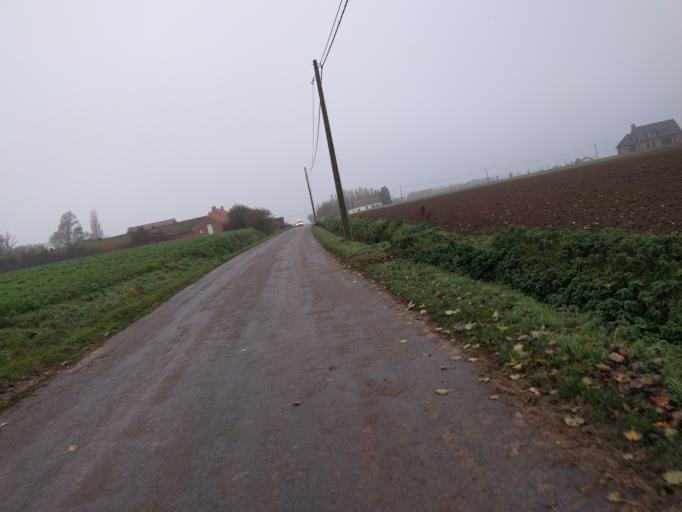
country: BE
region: Flanders
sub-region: Provincie West-Vlaanderen
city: Poperinge
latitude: 50.8186
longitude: 2.8040
